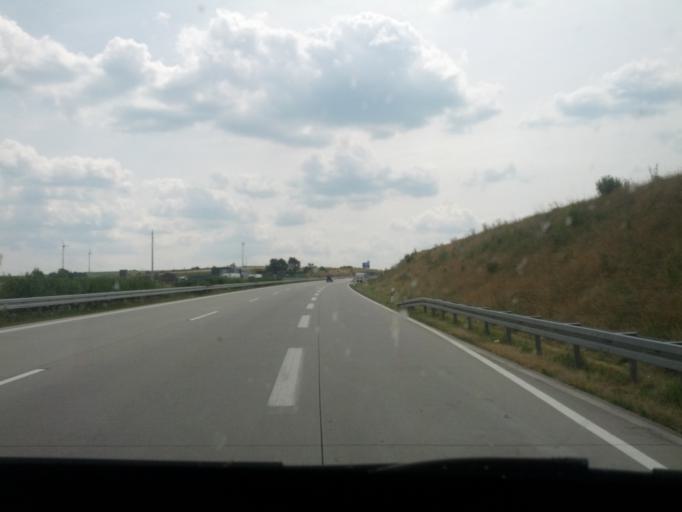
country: DE
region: Saxony
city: Liebstadt
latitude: 50.8247
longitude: 13.8876
